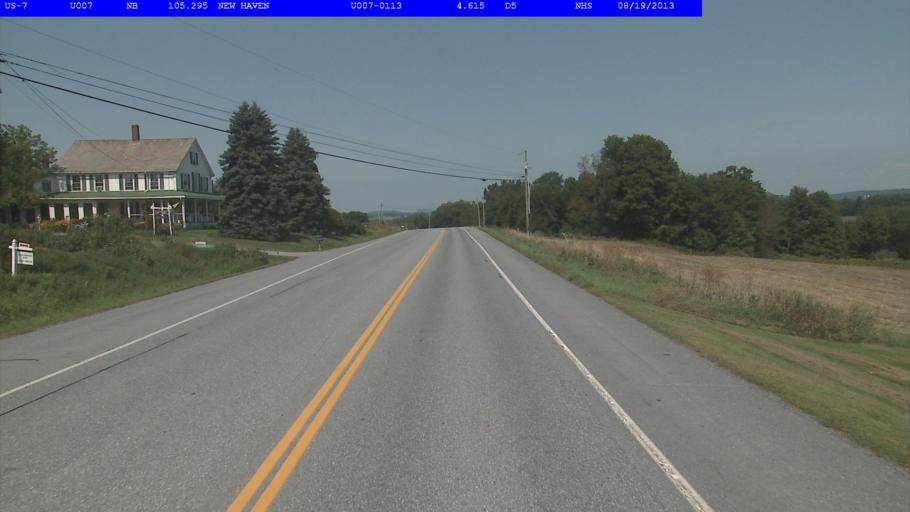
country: US
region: Vermont
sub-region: Addison County
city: Middlebury (village)
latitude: 44.1118
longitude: -73.1751
